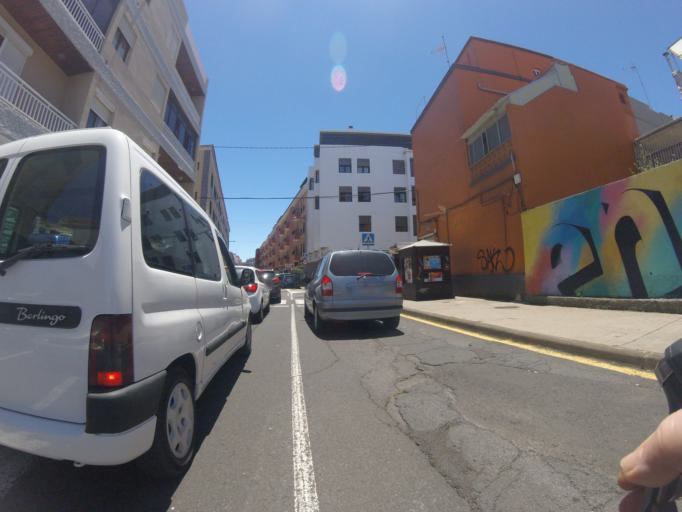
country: ES
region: Canary Islands
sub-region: Provincia de Santa Cruz de Tenerife
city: La Laguna
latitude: 28.4875
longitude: -16.3194
